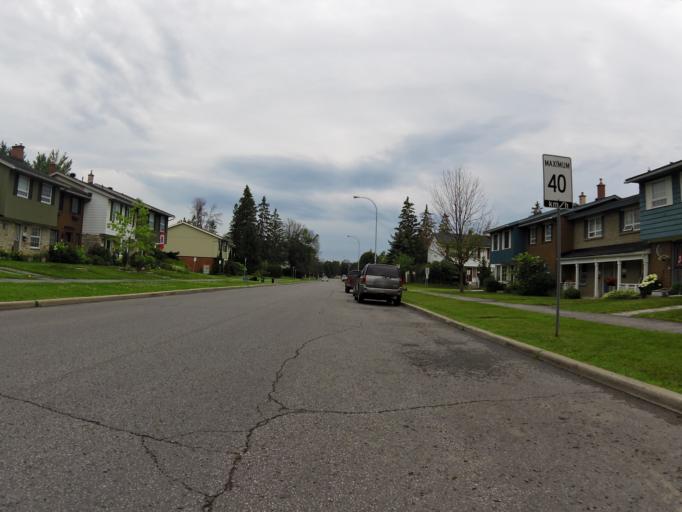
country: CA
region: Ontario
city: Bells Corners
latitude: 45.3397
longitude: -75.7876
